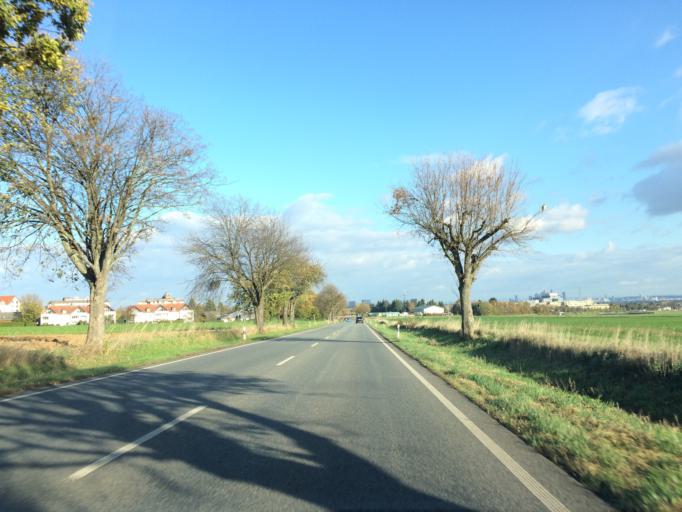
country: DE
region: Hesse
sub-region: Regierungsbezirk Darmstadt
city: Bad Soden am Taunus
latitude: 50.1314
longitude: 8.5013
